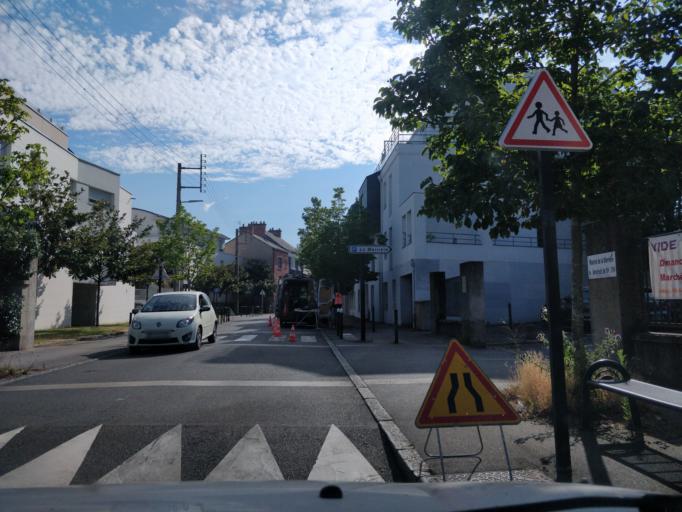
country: FR
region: Pays de la Loire
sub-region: Departement de la Loire-Atlantique
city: Nantes
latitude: 47.2340
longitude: -1.5312
